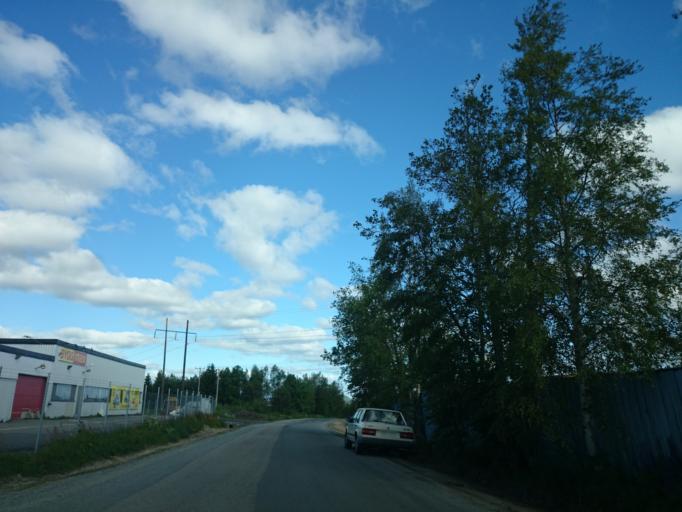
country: SE
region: Vaesternorrland
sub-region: Haernoesands Kommun
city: Haernoesand
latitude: 62.6504
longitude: 17.8946
